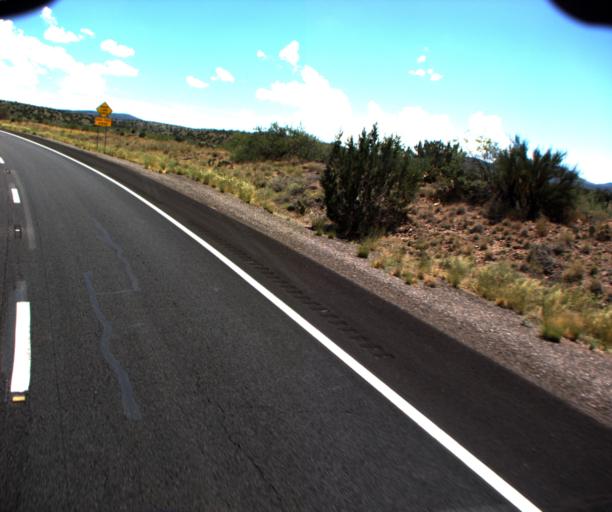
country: US
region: Arizona
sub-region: Yavapai County
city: Camp Verde
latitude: 34.5089
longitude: -111.7404
